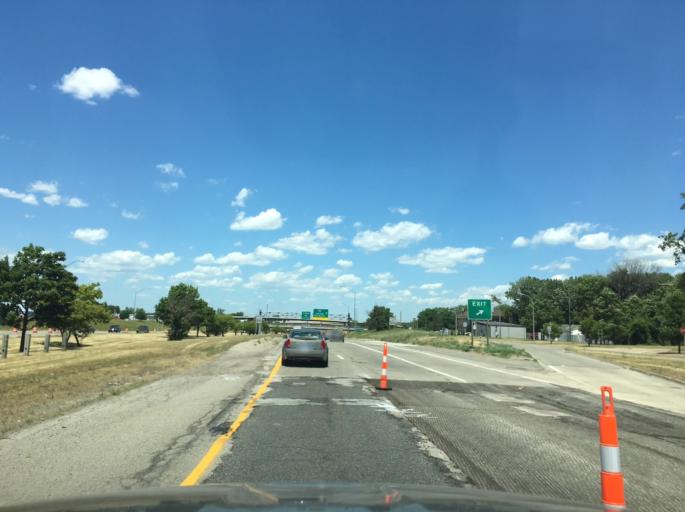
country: US
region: Michigan
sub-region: Macomb County
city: Warren
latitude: 42.4792
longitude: -83.0453
